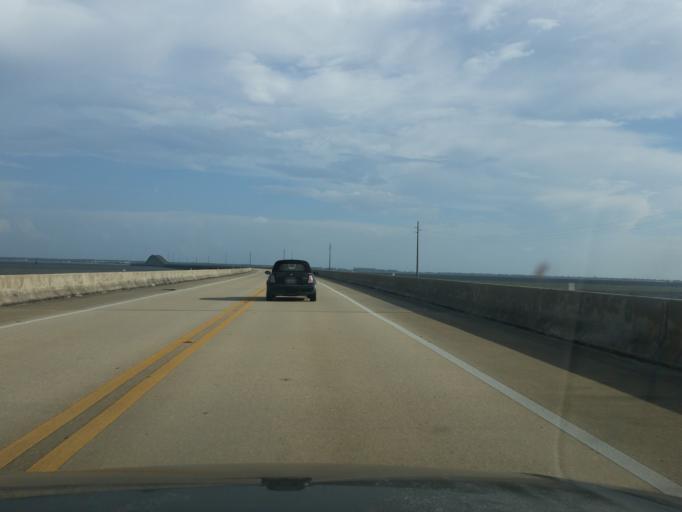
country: US
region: Alabama
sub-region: Mobile County
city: Dauphin Island
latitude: 30.3079
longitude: -88.1375
